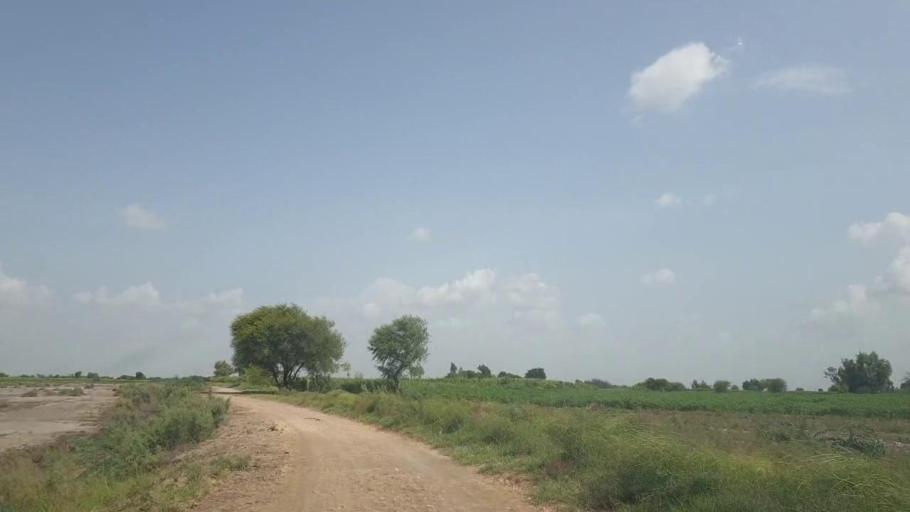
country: PK
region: Sindh
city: Tando Bago
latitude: 24.7520
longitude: 69.1758
